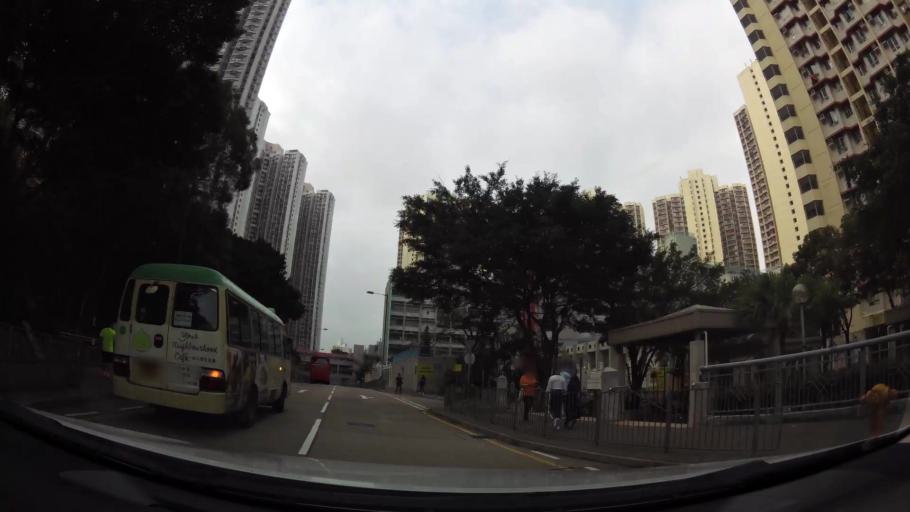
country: HK
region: Kowloon City
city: Kowloon
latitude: 22.3081
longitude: 114.2378
